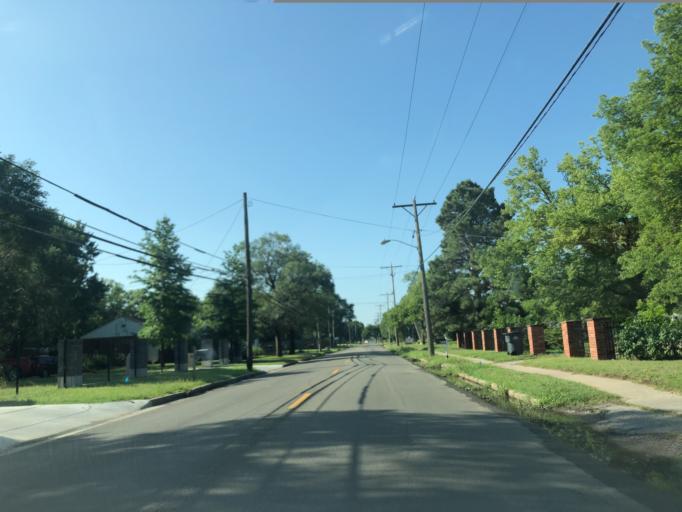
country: US
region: Kansas
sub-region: Sedgwick County
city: Park City
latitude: 37.7498
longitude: -97.3449
